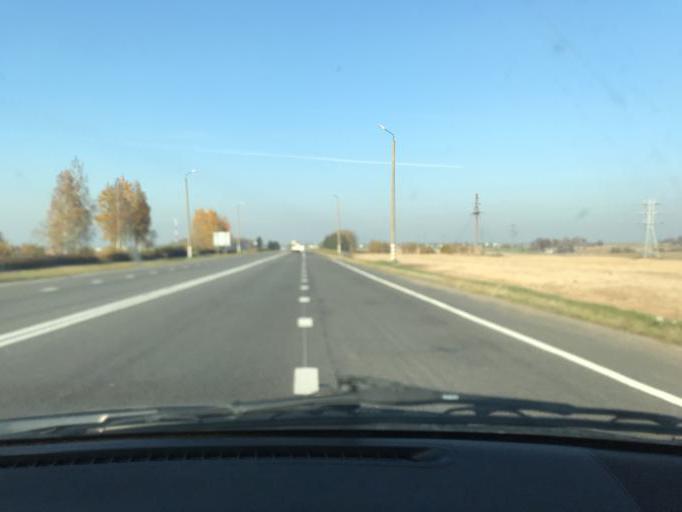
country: BY
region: Mogilev
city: Shklow
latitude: 54.2221
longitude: 30.4523
